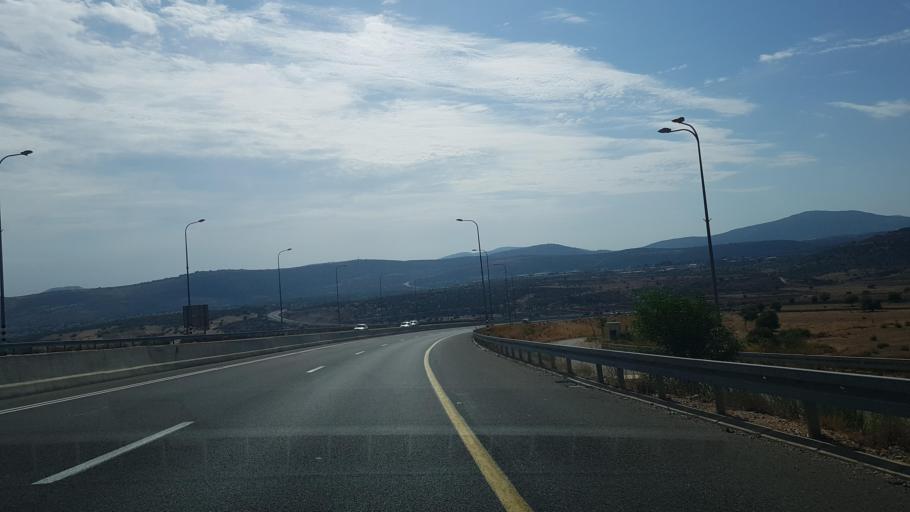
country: IL
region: Northern District
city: Maghar
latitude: 32.8882
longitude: 35.4789
